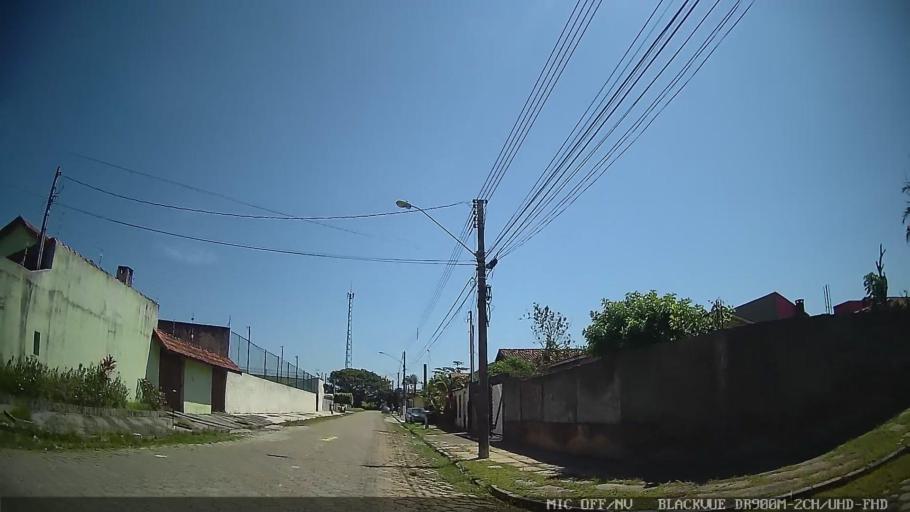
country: BR
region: Sao Paulo
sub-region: Peruibe
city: Peruibe
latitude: -24.2873
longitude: -46.9654
